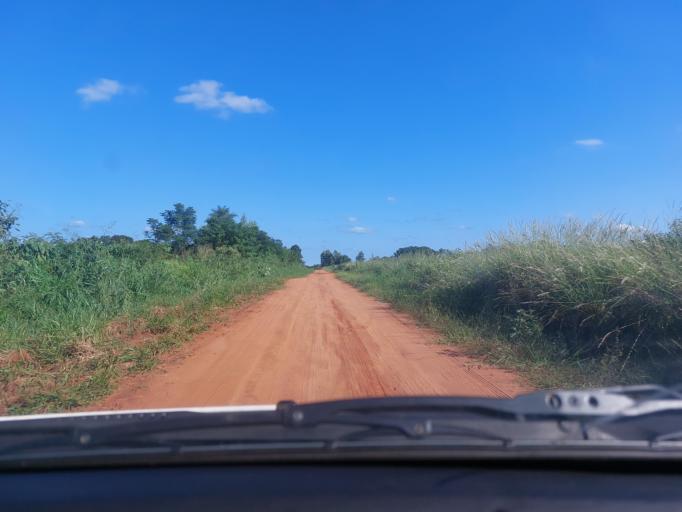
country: PY
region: San Pedro
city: Guayaybi
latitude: -24.5107
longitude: -56.5462
